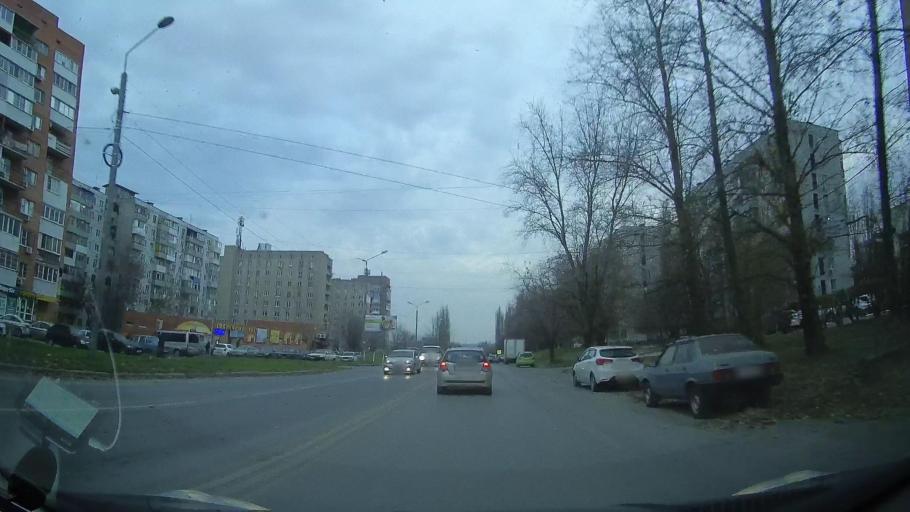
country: RU
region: Rostov
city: Severnyy
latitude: 47.3013
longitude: 39.7229
